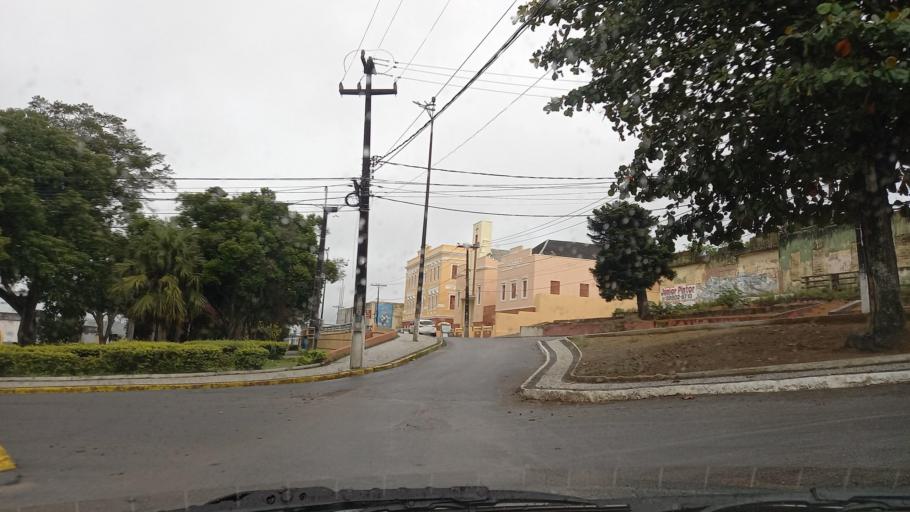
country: BR
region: Pernambuco
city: Garanhuns
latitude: -8.8884
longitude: -36.4948
